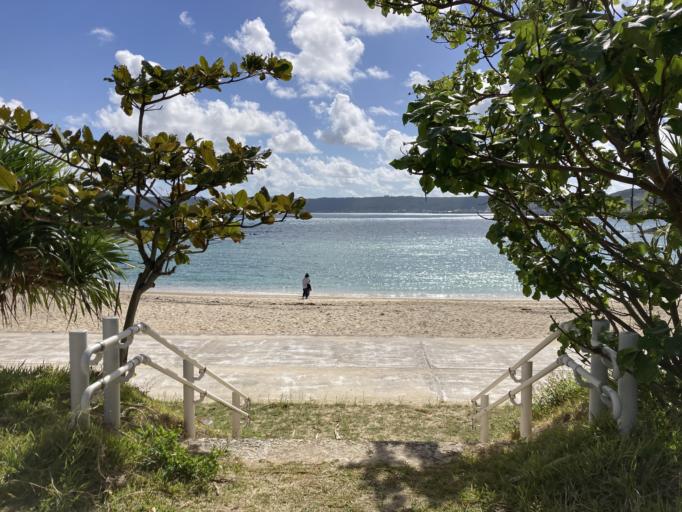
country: JP
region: Okinawa
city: Ginowan
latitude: 26.2125
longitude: 127.7717
